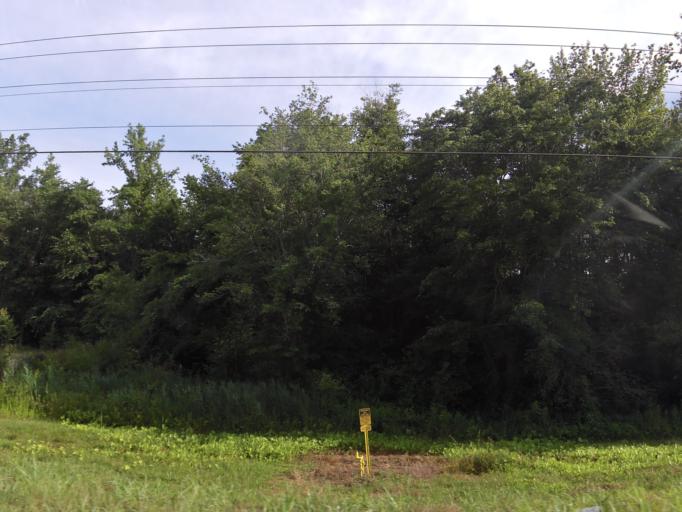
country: US
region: Tennessee
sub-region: Benton County
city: Camden
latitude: 36.0458
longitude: -88.1673
